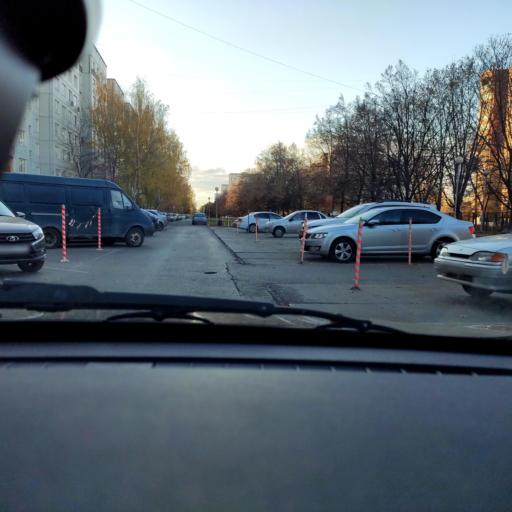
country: RU
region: Samara
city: Tol'yatti
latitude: 53.5240
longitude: 49.3174
